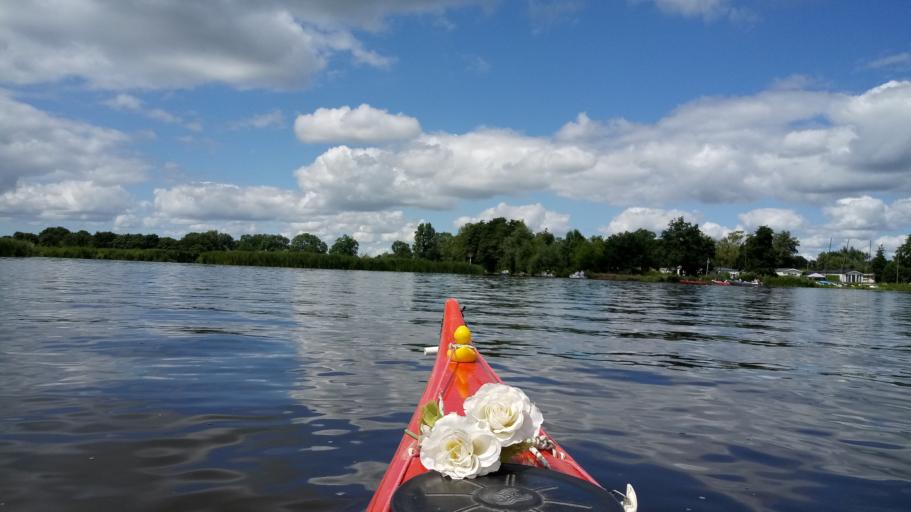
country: NL
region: Overijssel
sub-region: Gemeente Steenwijkerland
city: Wanneperveen
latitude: 52.7169
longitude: 6.0968
